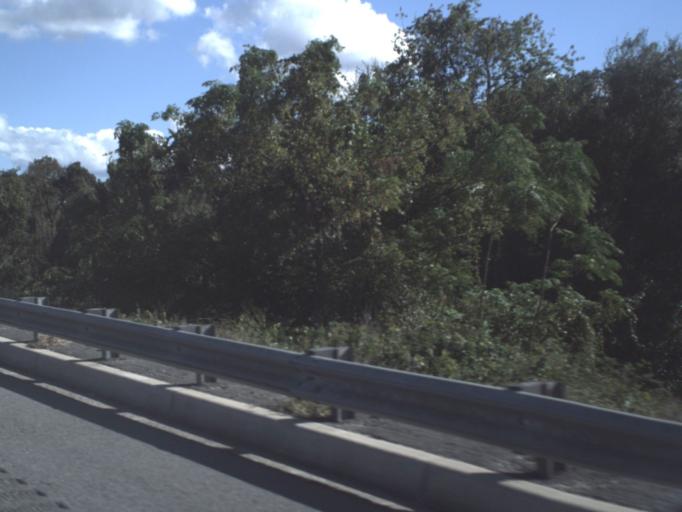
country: US
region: Florida
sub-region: Lake County
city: Montverde
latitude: 28.5597
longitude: -81.6796
